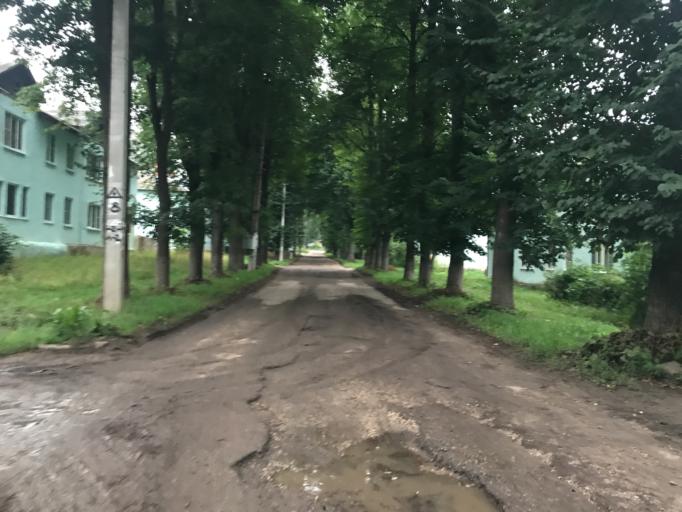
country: RU
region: Tula
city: Priupskiy
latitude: 53.9404
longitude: 37.7048
